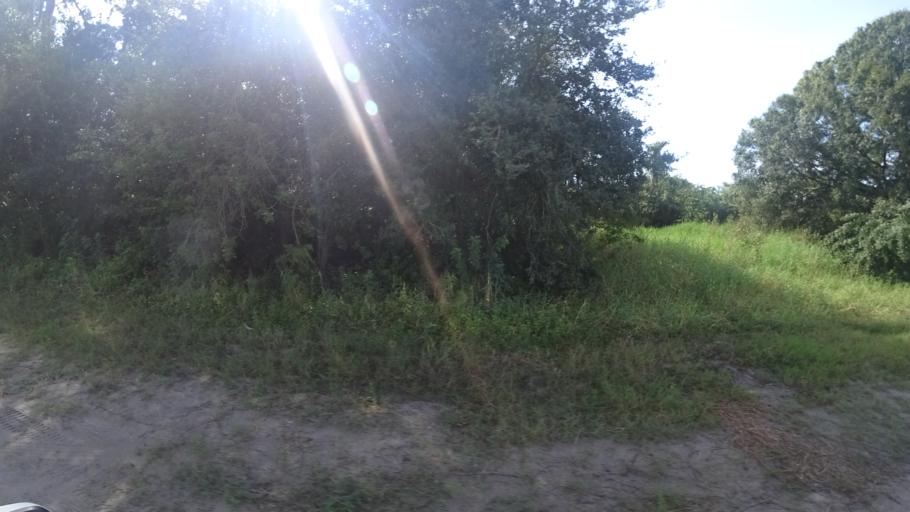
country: US
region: Florida
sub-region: Sarasota County
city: The Meadows
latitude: 27.4484
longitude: -82.3143
